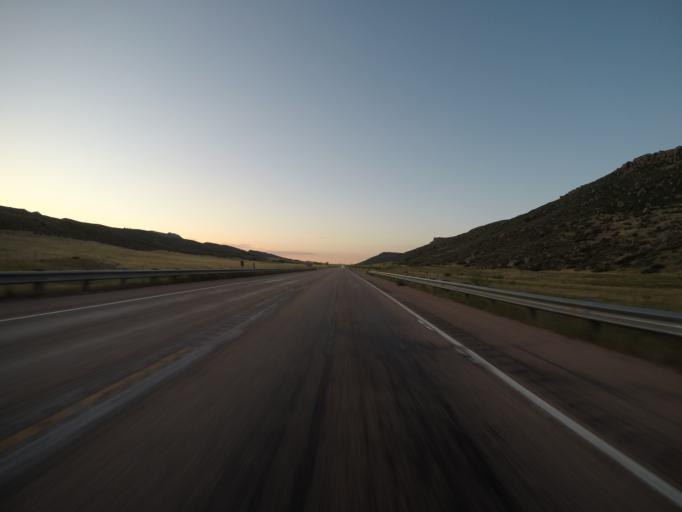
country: US
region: Colorado
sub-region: Larimer County
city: Laporte
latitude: 40.6946
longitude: -105.1749
